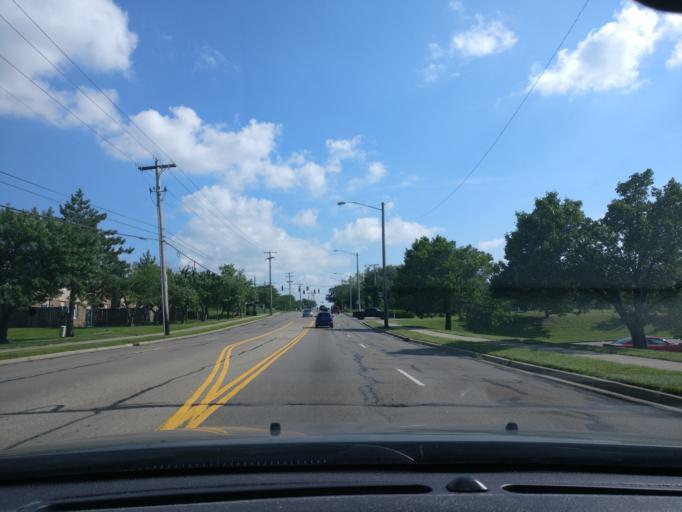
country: US
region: Ohio
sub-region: Montgomery County
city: West Carrollton City
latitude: 39.6465
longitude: -84.2431
